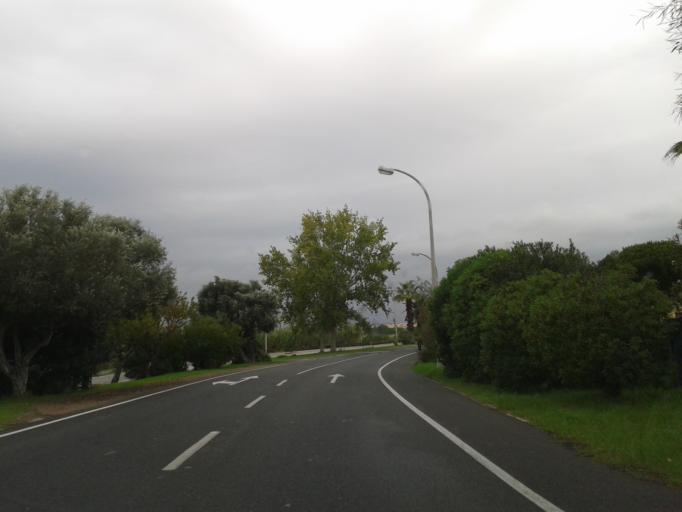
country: PT
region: Faro
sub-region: Loule
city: Vilamoura
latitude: 37.0922
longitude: -8.1270
